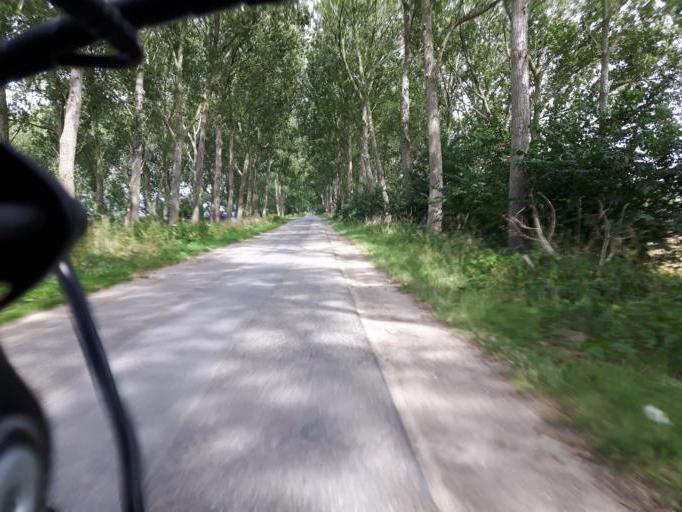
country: NL
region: North Brabant
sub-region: Gemeente Steenbergen
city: Steenbergen
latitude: 51.6002
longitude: 4.2889
